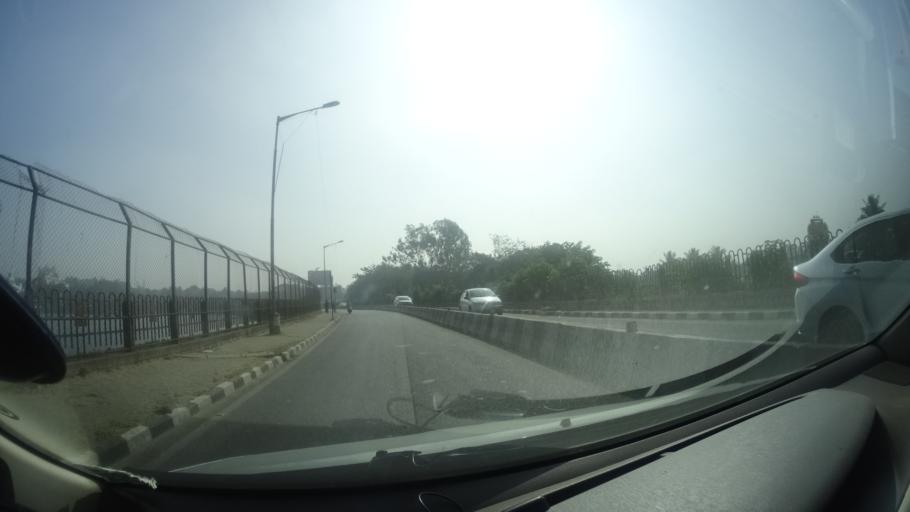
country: IN
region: Karnataka
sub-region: Bangalore Urban
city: Bangalore
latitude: 13.0078
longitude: 77.5727
